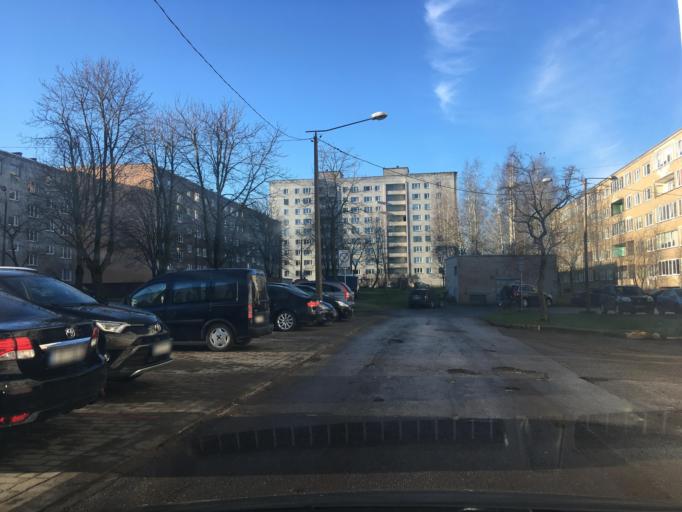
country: EE
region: Ida-Virumaa
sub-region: Narva linn
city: Narva
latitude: 59.3829
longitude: 28.1766
